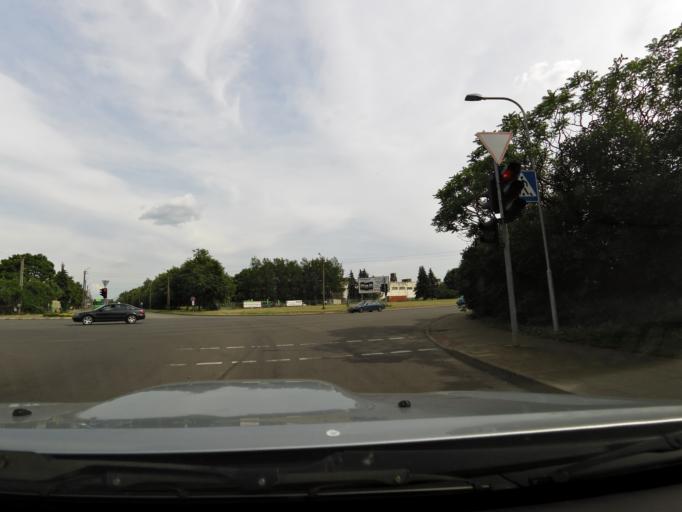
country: LT
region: Marijampoles apskritis
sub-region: Marijampole Municipality
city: Marijampole
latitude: 54.5752
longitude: 23.3702
